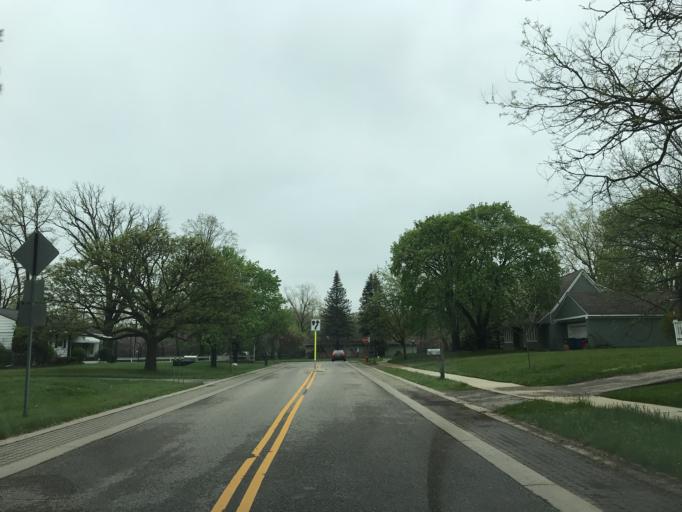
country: US
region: Michigan
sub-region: Washtenaw County
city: Ann Arbor
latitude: 42.2457
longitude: -83.7081
